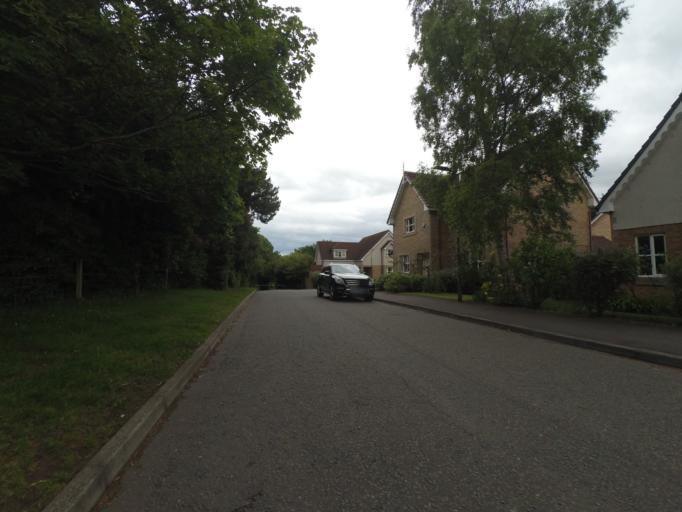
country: GB
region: Scotland
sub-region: East Lothian
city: Musselburgh
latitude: 55.9297
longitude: -3.0566
